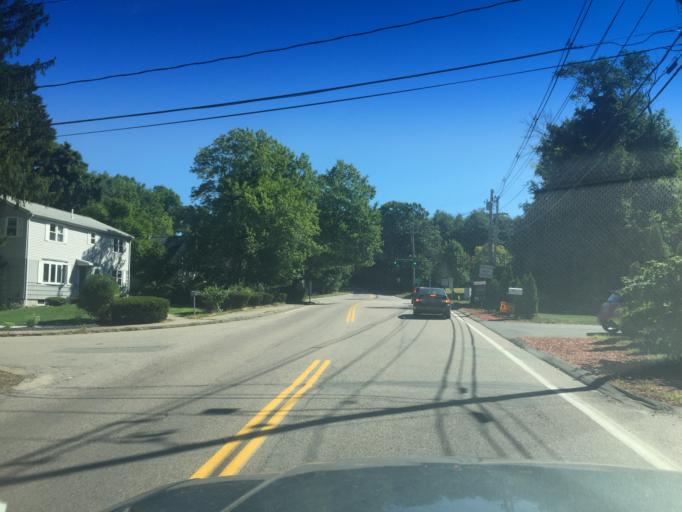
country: US
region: Massachusetts
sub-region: Norfolk County
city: Sharon
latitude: 42.1442
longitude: -71.2004
